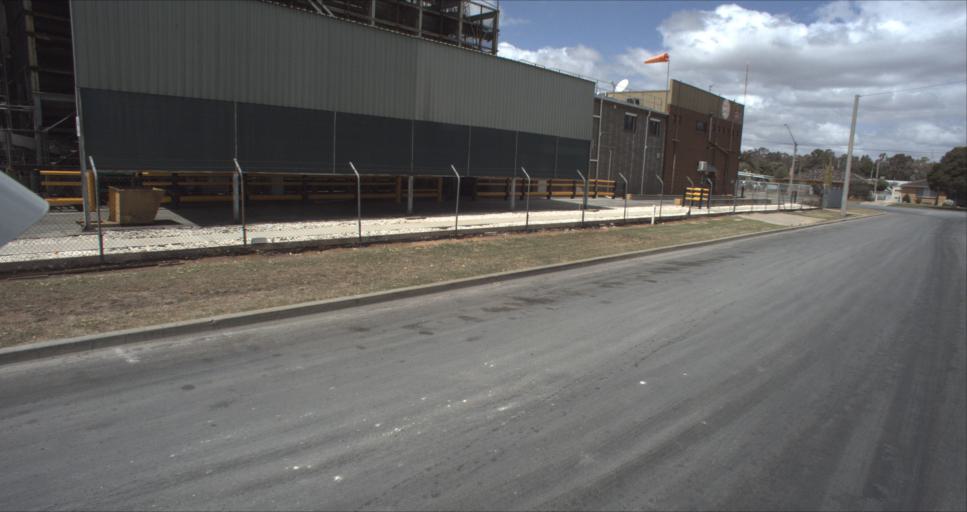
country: AU
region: New South Wales
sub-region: Leeton
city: Leeton
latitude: -34.5524
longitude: 146.3878
